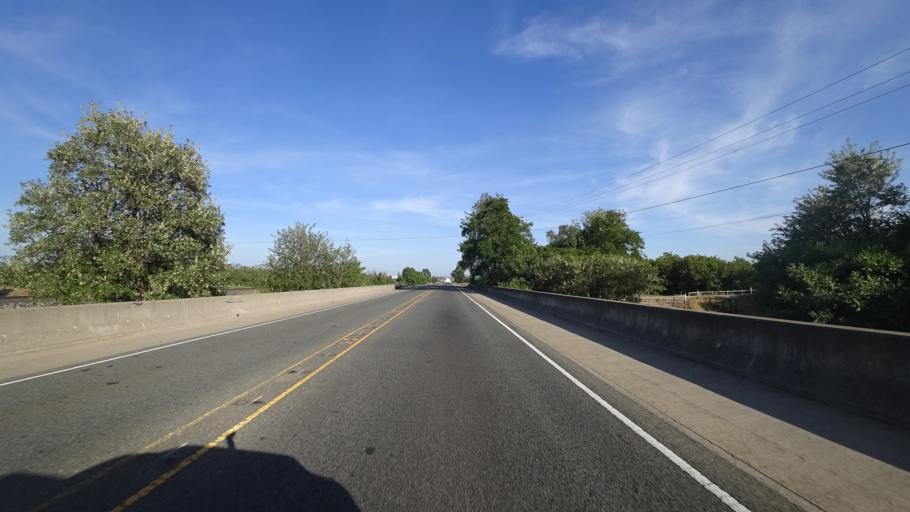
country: US
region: California
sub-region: Yuba County
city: Wheatland
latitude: 38.9994
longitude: -121.4057
